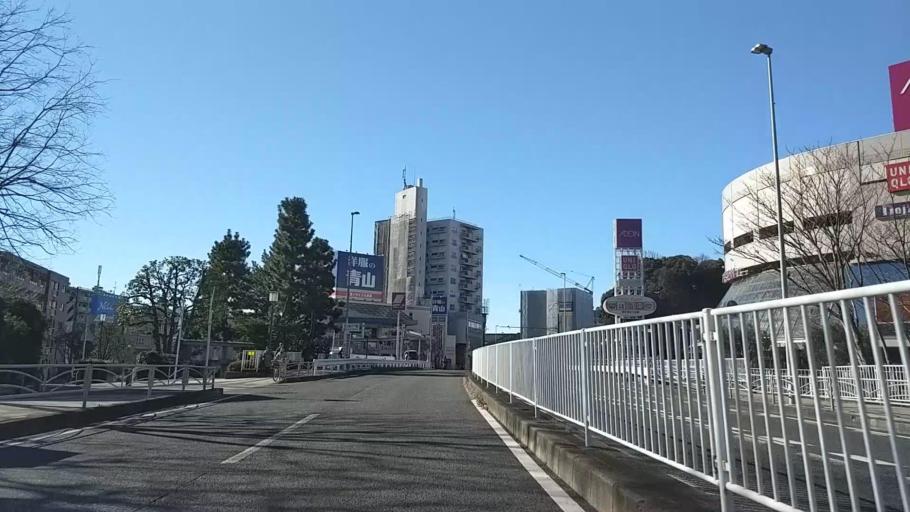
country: JP
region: Kanagawa
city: Zushi
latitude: 35.3340
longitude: 139.6237
